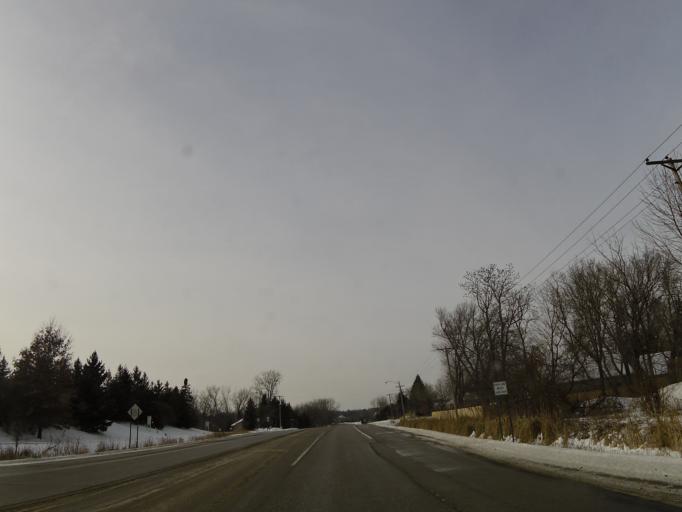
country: US
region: Minnesota
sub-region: Hennepin County
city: Shorewood
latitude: 44.8893
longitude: -93.6144
